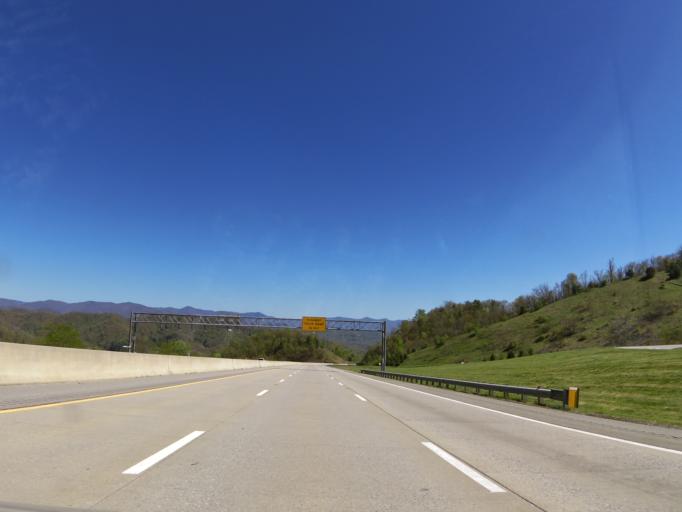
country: US
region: North Carolina
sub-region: Madison County
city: Mars Hill
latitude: 35.8749
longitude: -82.5434
